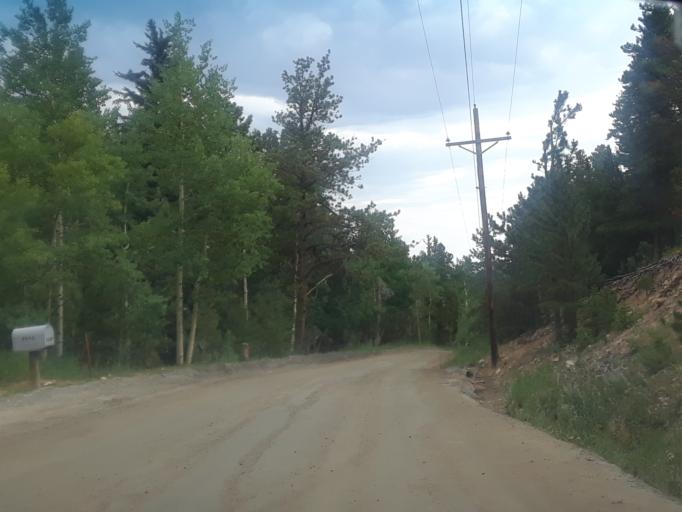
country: US
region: Colorado
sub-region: Boulder County
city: Nederland
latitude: 40.0614
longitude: -105.4146
